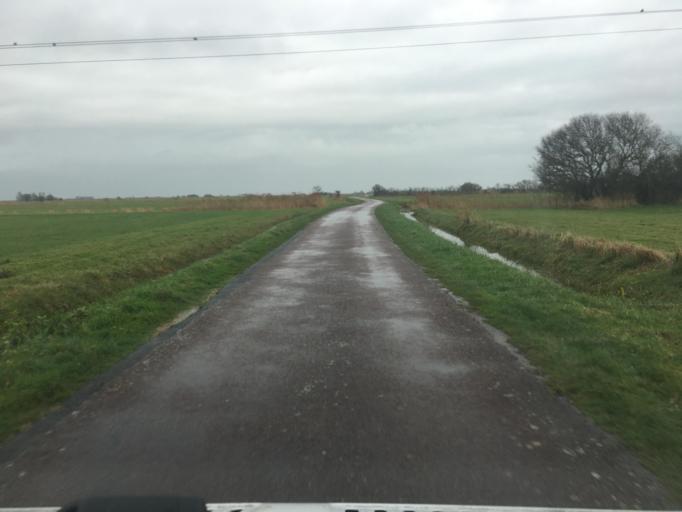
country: FR
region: Lower Normandy
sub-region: Departement de la Manche
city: Sainte-Mere-Eglise
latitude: 49.4438
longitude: -1.2432
